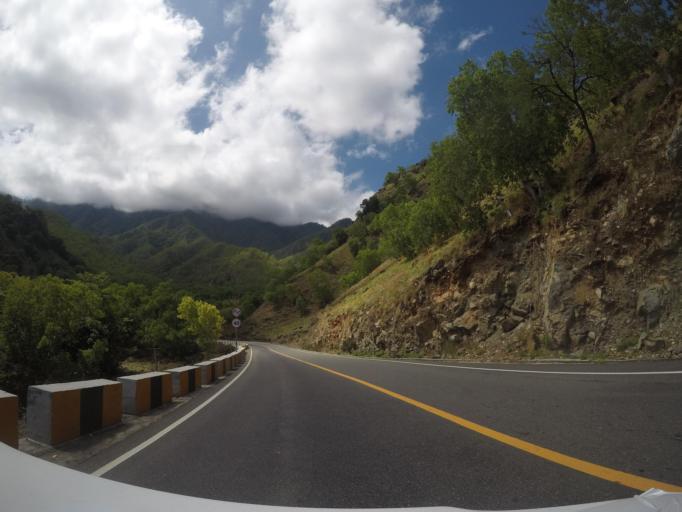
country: TL
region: Manatuto
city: Manatuto
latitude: -8.4782
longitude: 125.9071
